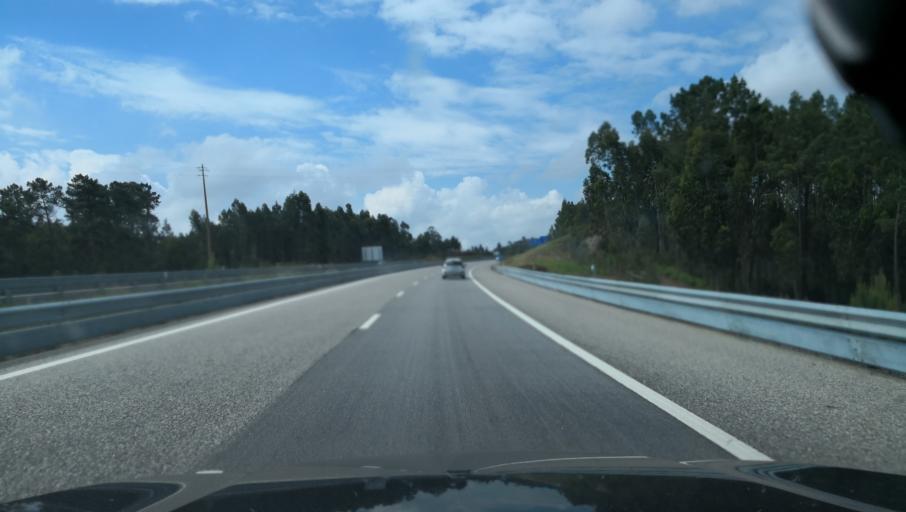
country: PT
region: Leiria
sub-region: Leiria
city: Amor
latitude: 39.7537
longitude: -8.8763
